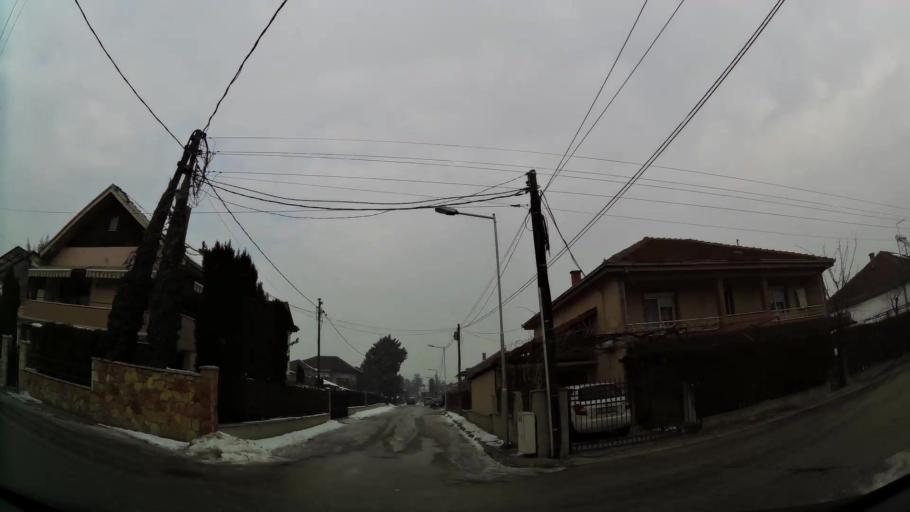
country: MK
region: Saraj
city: Saraj
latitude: 42.0234
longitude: 21.3541
